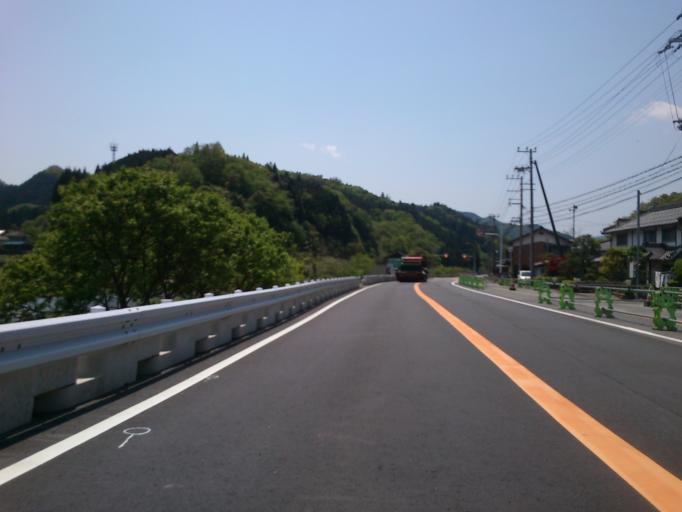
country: JP
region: Kyoto
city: Fukuchiyama
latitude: 35.3313
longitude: 135.0691
